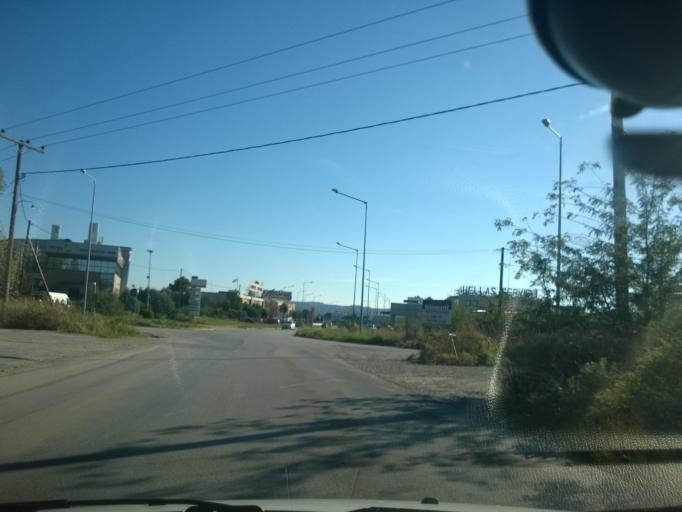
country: GR
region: Central Macedonia
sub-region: Nomos Thessalonikis
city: Thermi
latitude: 40.5330
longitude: 23.0140
